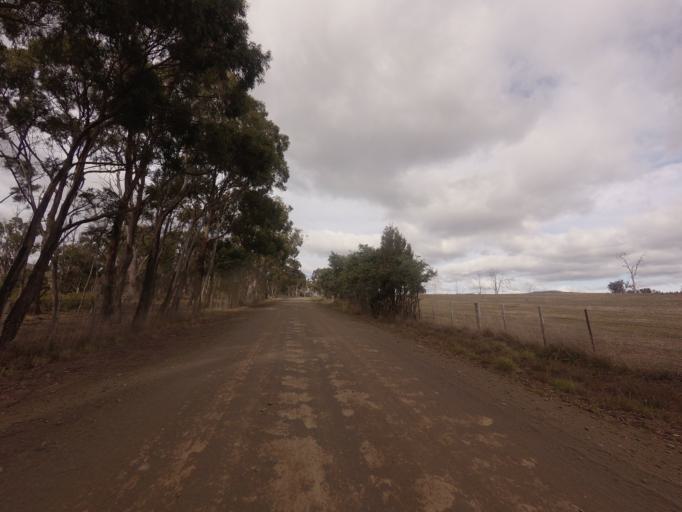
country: AU
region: Tasmania
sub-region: Brighton
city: Bridgewater
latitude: -42.4585
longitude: 147.2537
